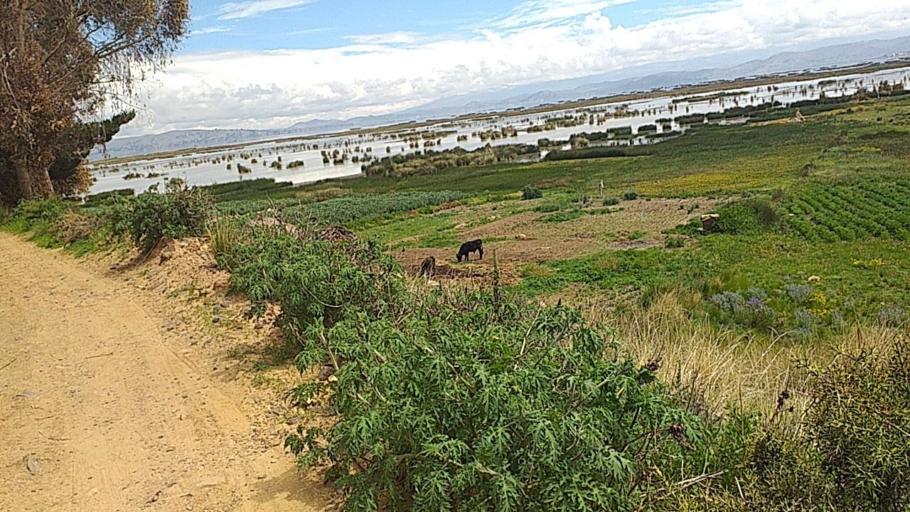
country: BO
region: La Paz
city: Batallas
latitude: -16.3275
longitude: -68.6429
